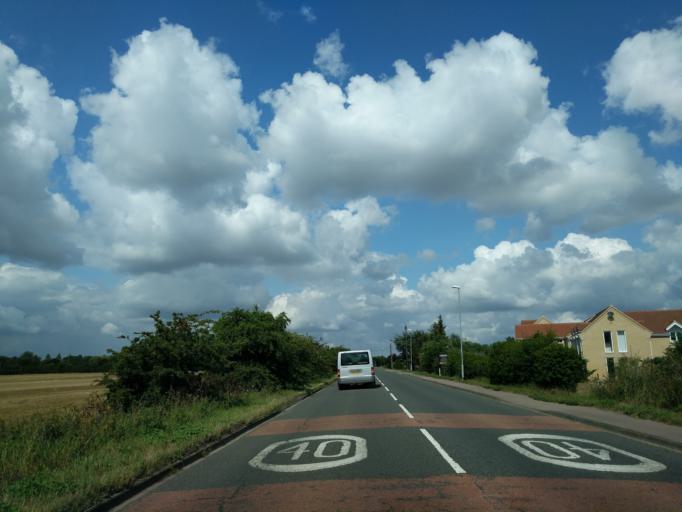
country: GB
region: England
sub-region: Cambridgeshire
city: Soham
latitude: 52.3128
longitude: 0.3774
